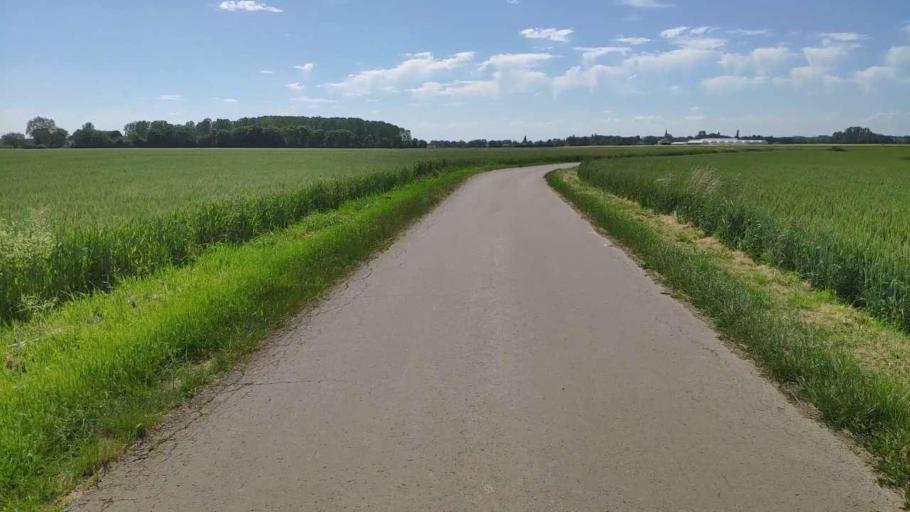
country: FR
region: Franche-Comte
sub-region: Departement du Jura
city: Bletterans
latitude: 46.7317
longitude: 5.4884
